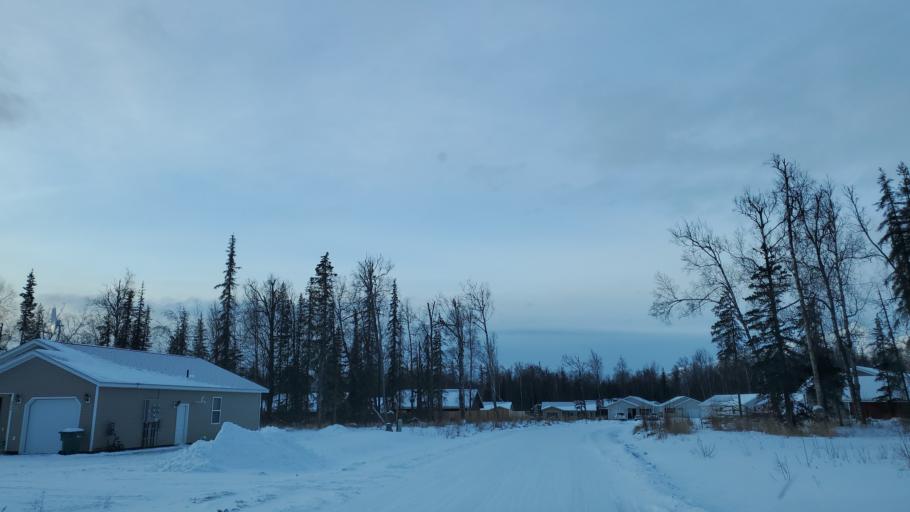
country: US
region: Alaska
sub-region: Matanuska-Susitna Borough
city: Fishhook
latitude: 61.6833
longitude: -149.2423
